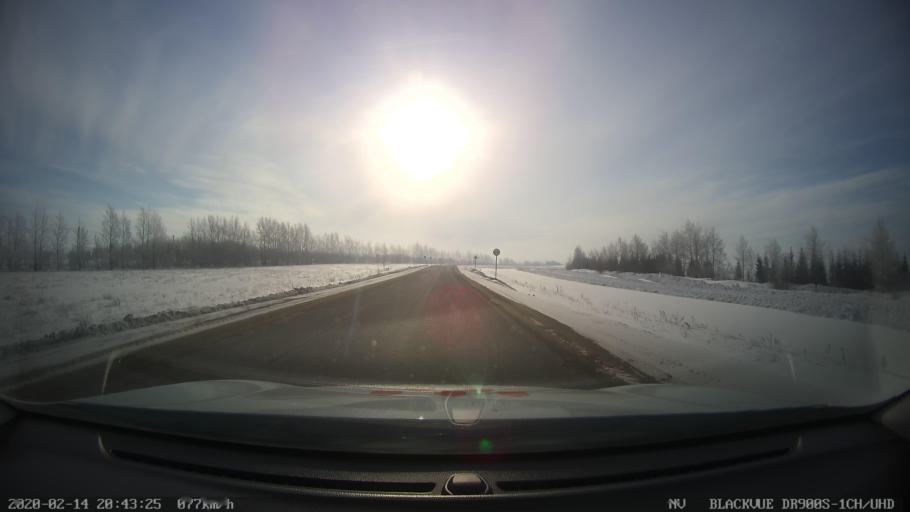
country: RU
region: Tatarstan
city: Kuybyshevskiy Zaton
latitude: 55.3083
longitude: 49.1477
